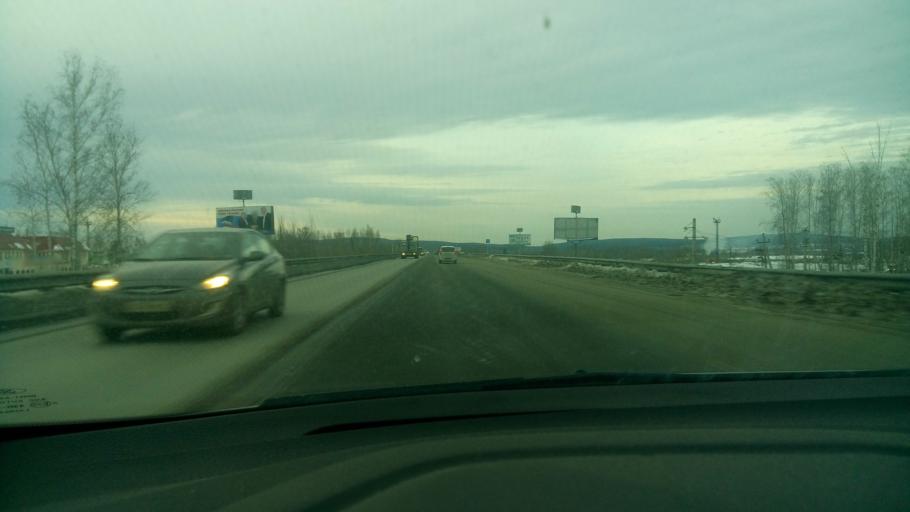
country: RU
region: Sverdlovsk
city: Istok
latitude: 56.7545
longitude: 60.7589
